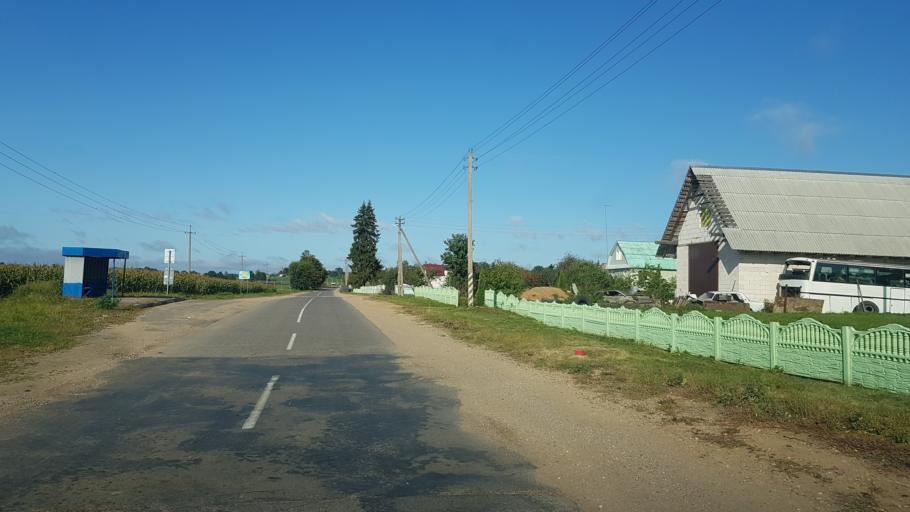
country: BY
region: Minsk
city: Dzyarzhynsk
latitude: 53.7364
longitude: 27.2095
